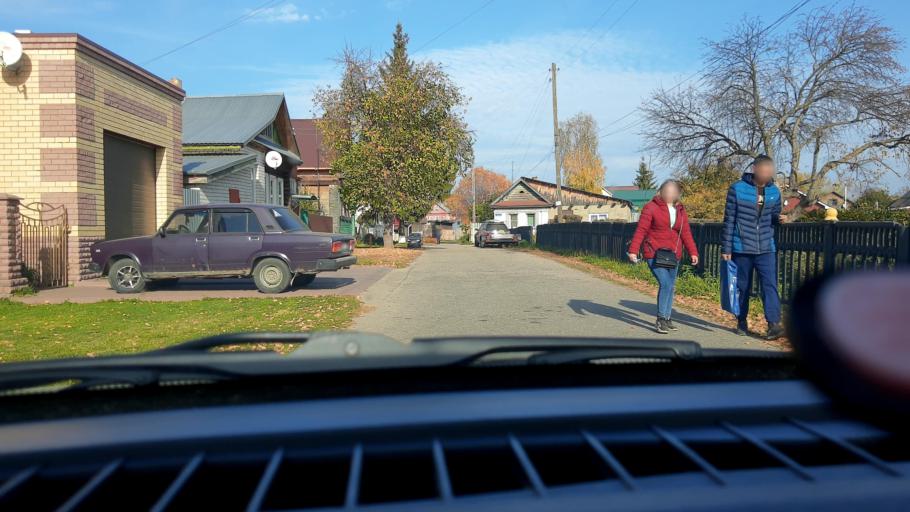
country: RU
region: Nizjnij Novgorod
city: Gorodets
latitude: 56.6415
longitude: 43.4706
